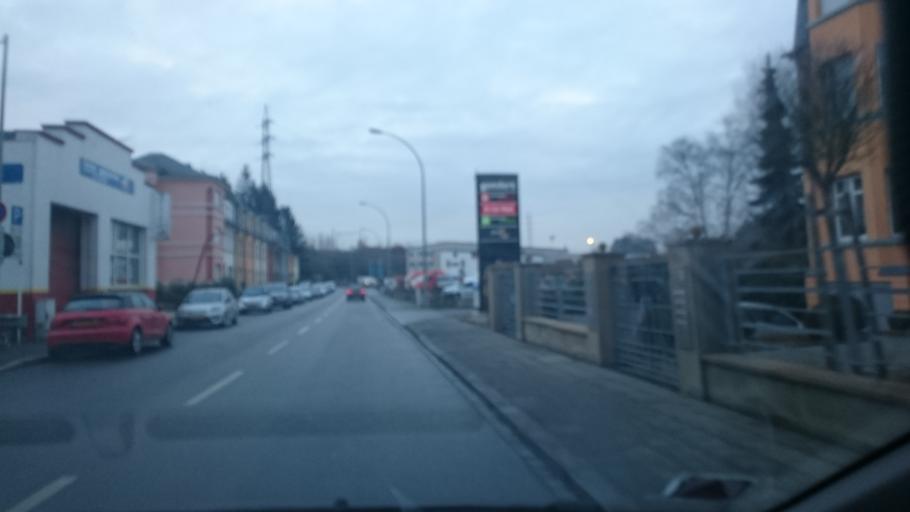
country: LU
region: Luxembourg
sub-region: Canton de Luxembourg
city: Luxembourg
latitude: 49.5975
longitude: 6.1170
